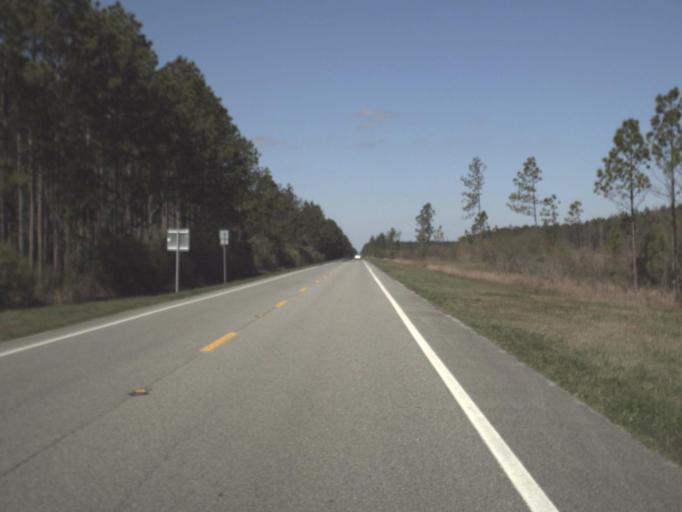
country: US
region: Florida
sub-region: Gulf County
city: Port Saint Joe
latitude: 29.9119
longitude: -85.2042
